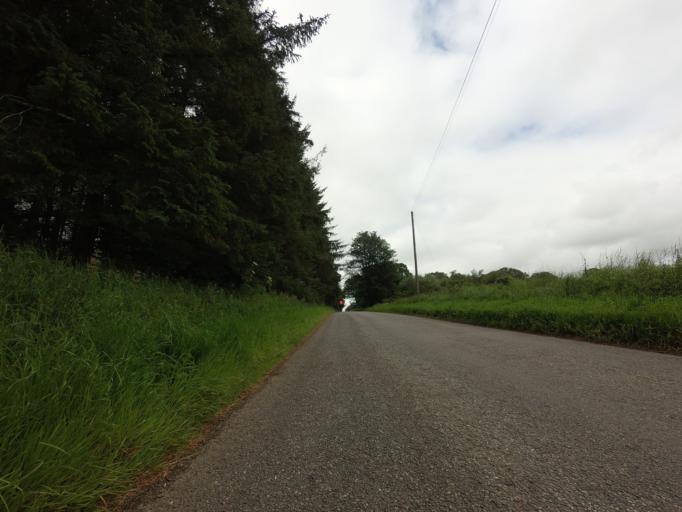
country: GB
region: Scotland
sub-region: Aberdeenshire
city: Mintlaw
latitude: 57.5303
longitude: -2.1506
